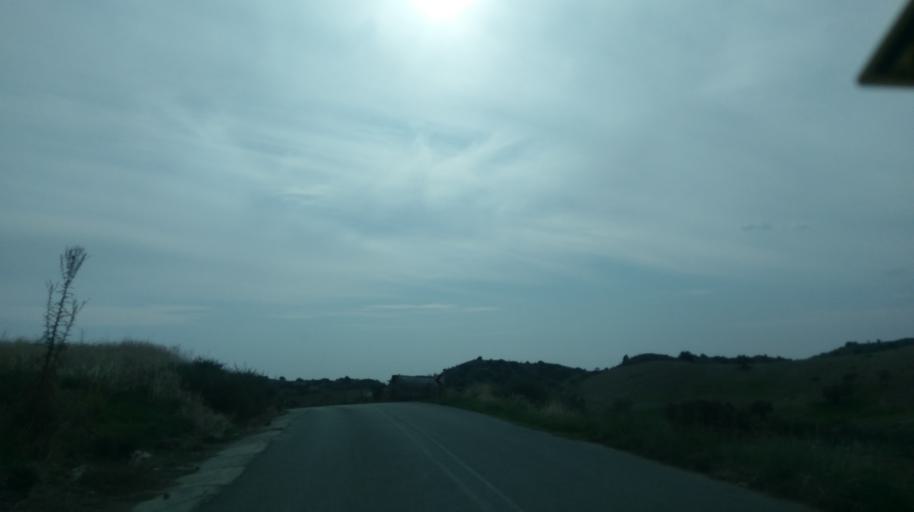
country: CY
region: Ammochostos
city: Trikomo
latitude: 35.3489
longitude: 33.9308
